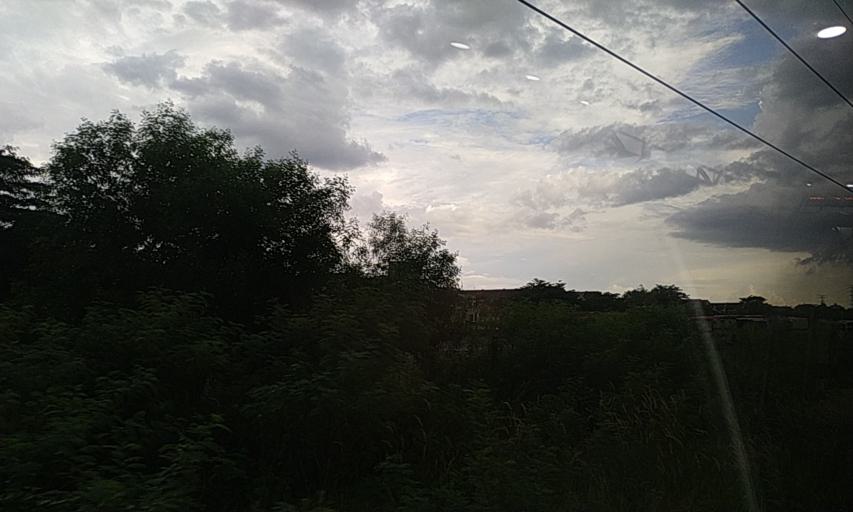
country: MY
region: Kuala Lumpur
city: Kuala Lumpur
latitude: 3.2199
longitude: 101.6725
